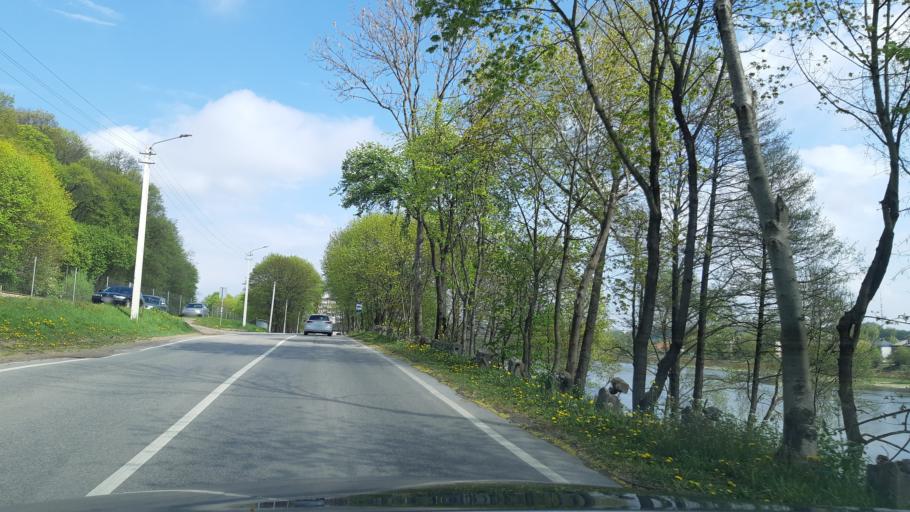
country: LT
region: Kauno apskritis
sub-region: Kaunas
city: Aleksotas
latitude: 54.8702
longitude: 23.9251
